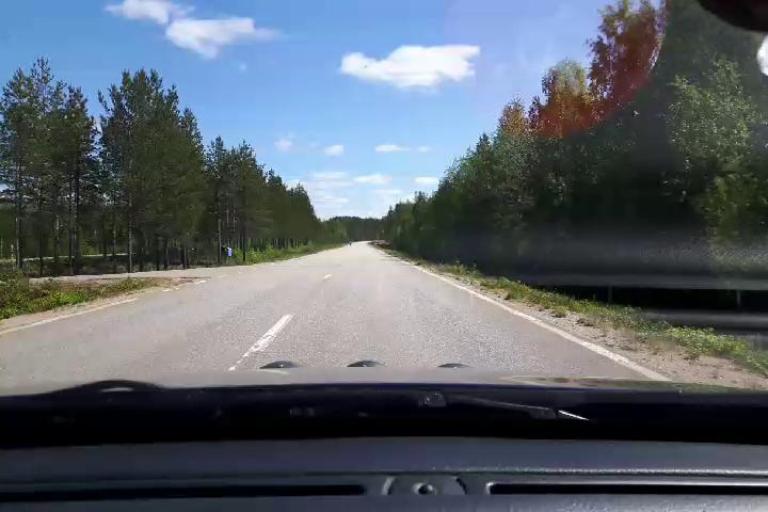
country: SE
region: Vaesternorrland
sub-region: Ange Kommun
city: Ange
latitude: 62.0558
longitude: 15.1310
